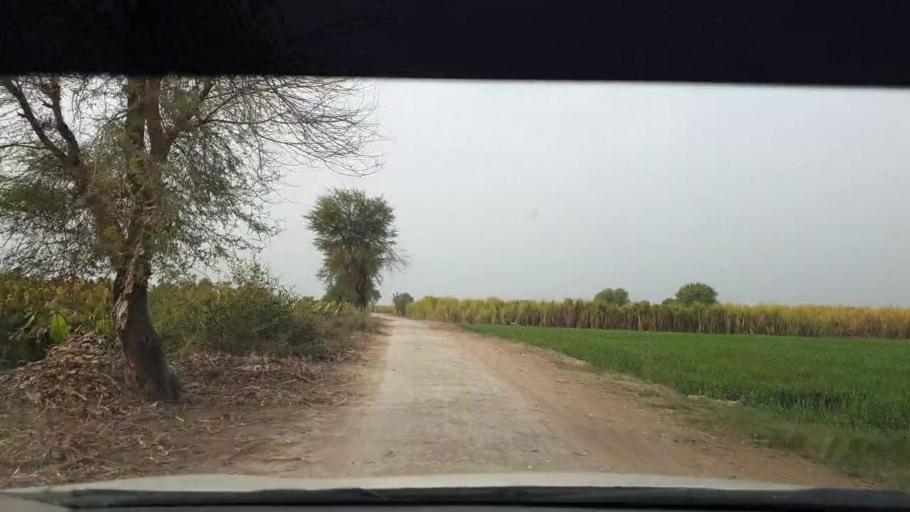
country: PK
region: Sindh
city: Jhol
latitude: 25.9083
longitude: 68.7748
